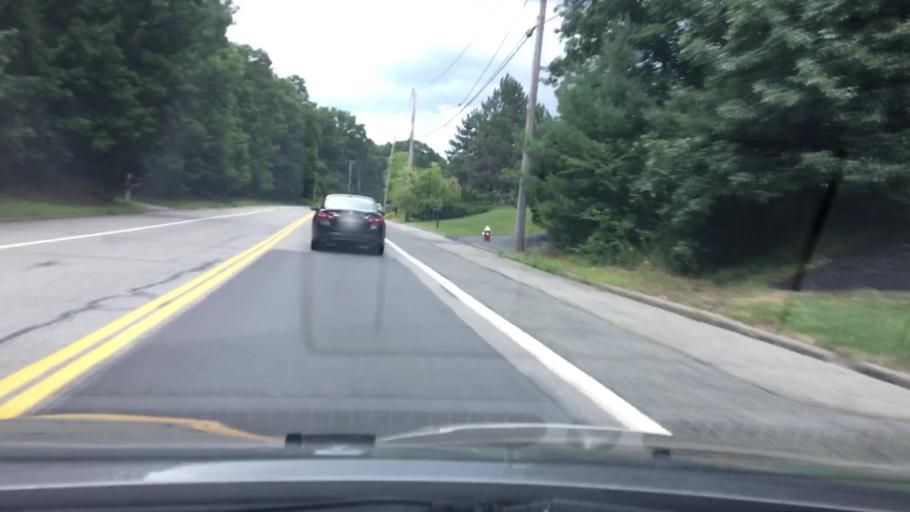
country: US
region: Rhode Island
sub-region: Providence County
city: Cumberland
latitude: 41.9713
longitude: -71.3788
